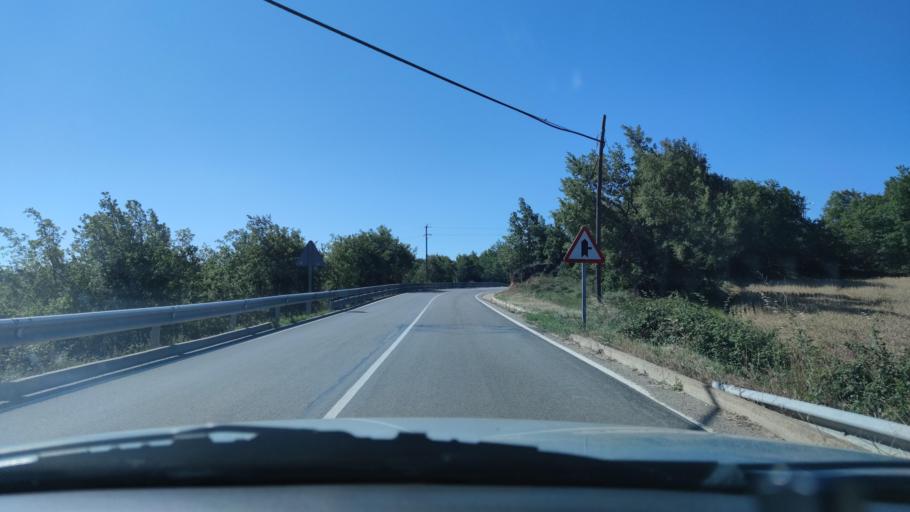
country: ES
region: Catalonia
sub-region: Provincia de Lleida
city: Solsona
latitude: 41.9208
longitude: 1.4986
